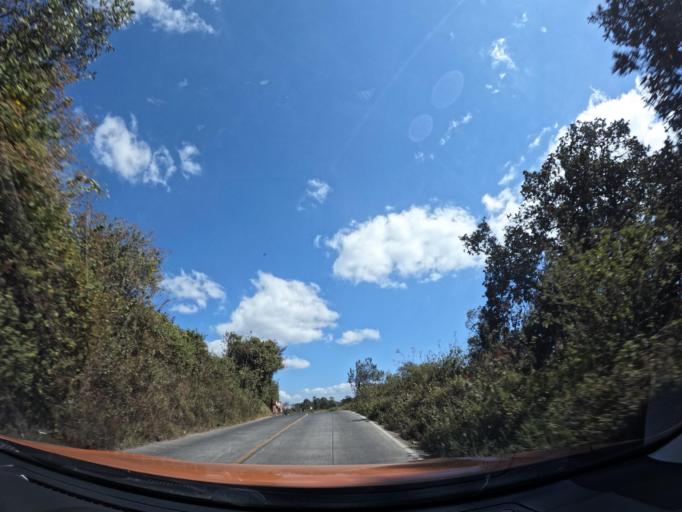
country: GT
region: Chimaltenango
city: Patzun
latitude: 14.6535
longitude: -91.0494
